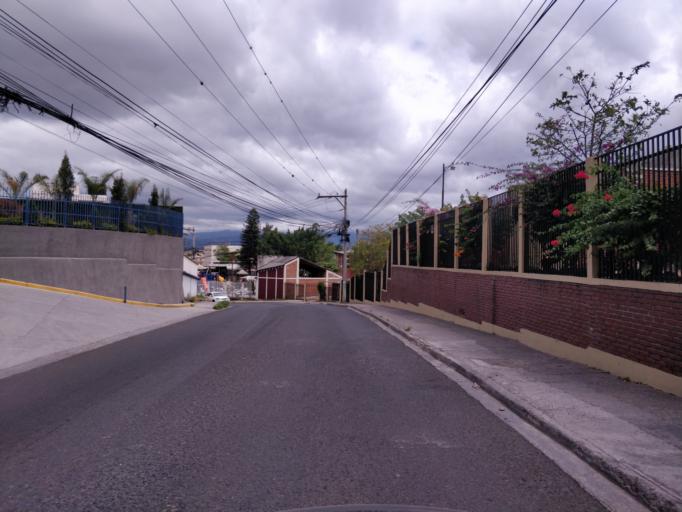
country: HN
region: Francisco Morazan
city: Yaguacire
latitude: 14.0455
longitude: -87.2208
